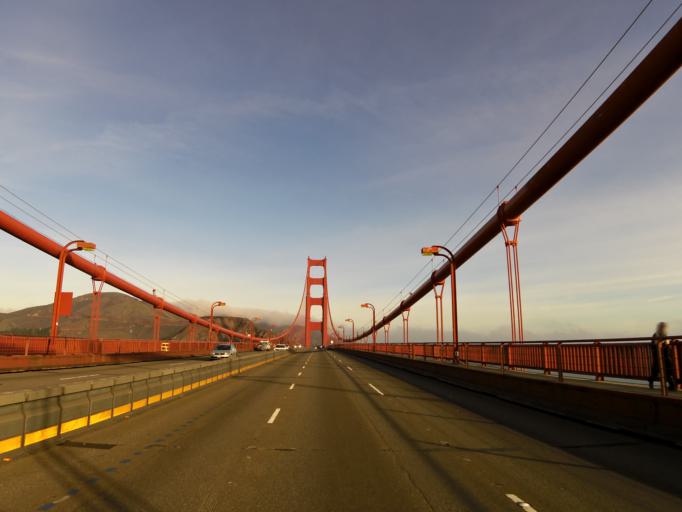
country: US
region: California
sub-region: Marin County
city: Sausalito
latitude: 37.8179
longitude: -122.4795
